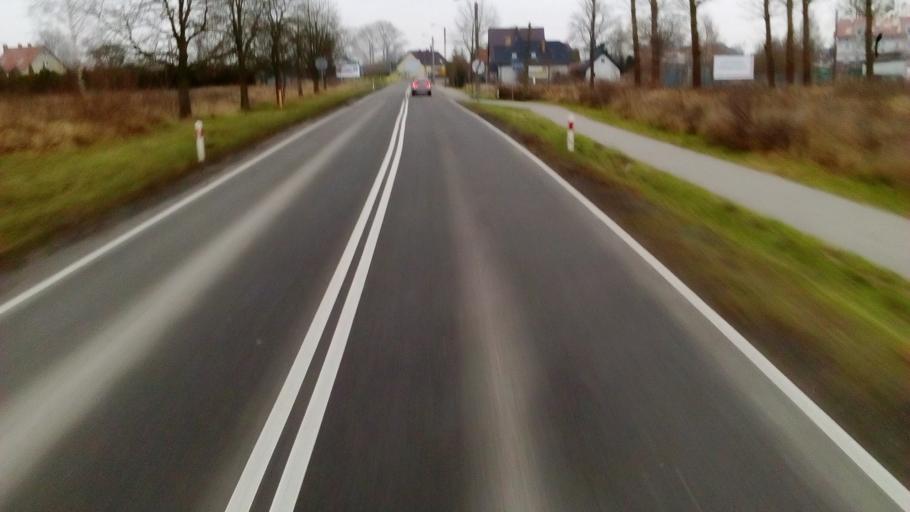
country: PL
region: West Pomeranian Voivodeship
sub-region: Powiat policki
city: Dobra
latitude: 53.4407
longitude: 14.4073
